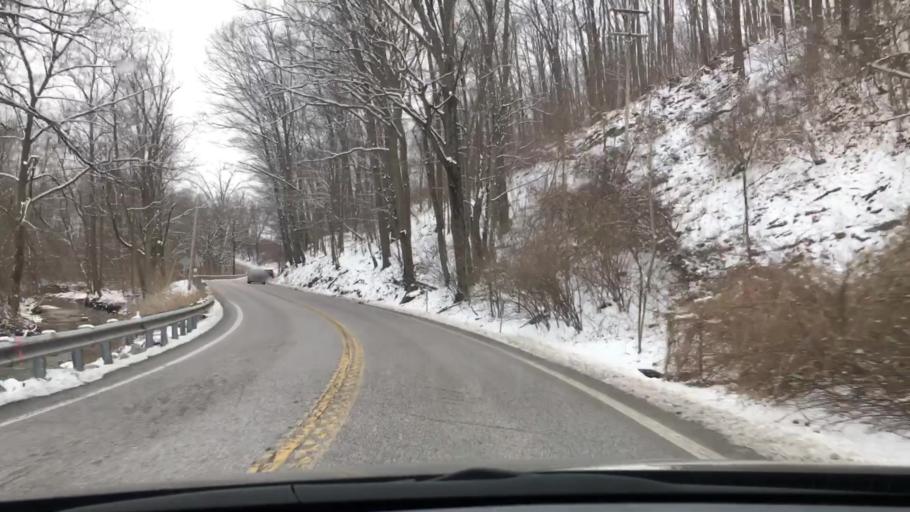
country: US
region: Pennsylvania
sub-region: York County
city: Yoe
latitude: 39.9258
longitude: -76.6487
